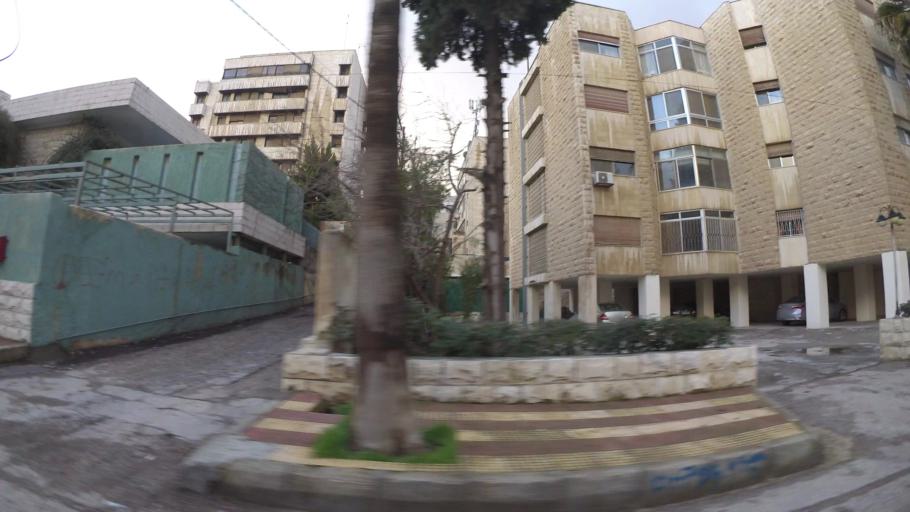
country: JO
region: Amman
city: Amman
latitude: 31.9602
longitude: 35.8891
